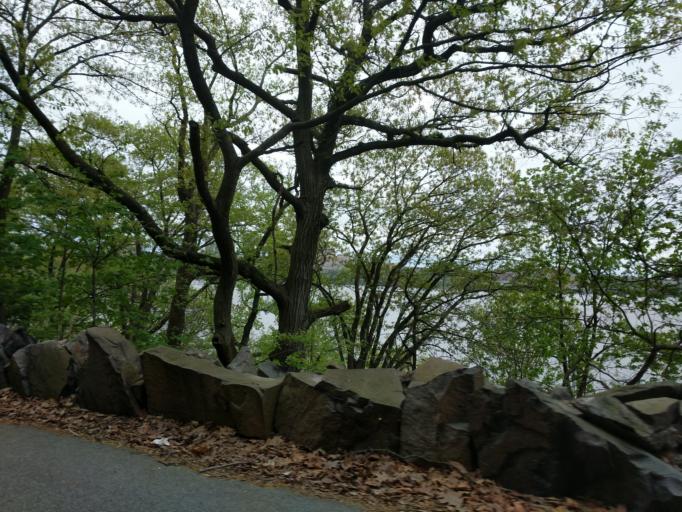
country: US
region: New Jersey
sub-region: Bergen County
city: Fort Lee
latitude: 40.8467
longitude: -73.9643
